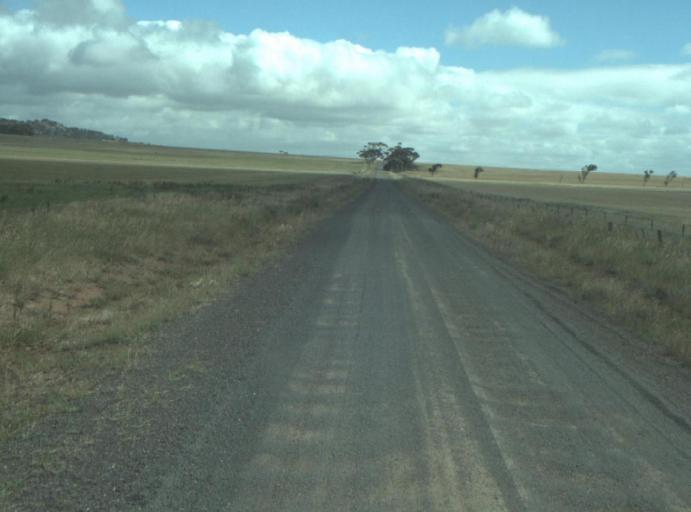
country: AU
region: Victoria
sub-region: Greater Geelong
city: Lara
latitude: -37.9059
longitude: 144.3165
